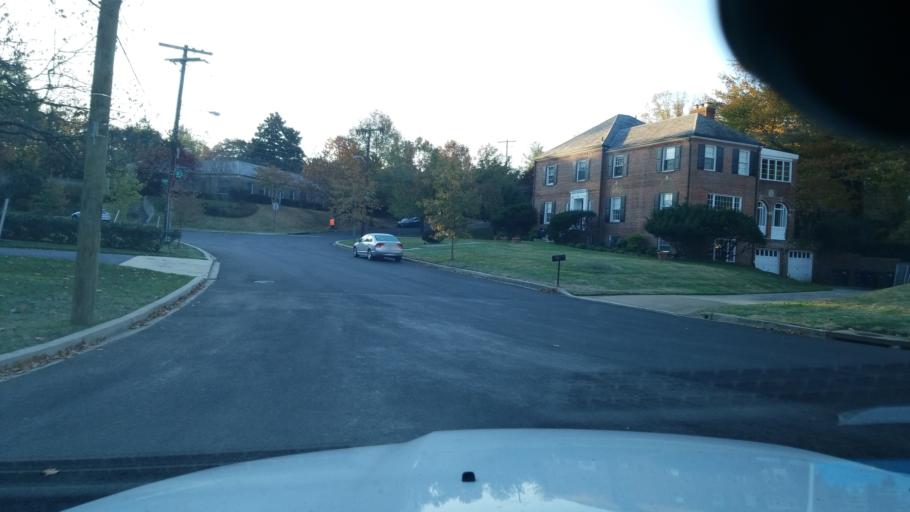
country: US
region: Maryland
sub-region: Montgomery County
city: Chevy Chase Village
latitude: 38.9547
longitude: -77.0656
